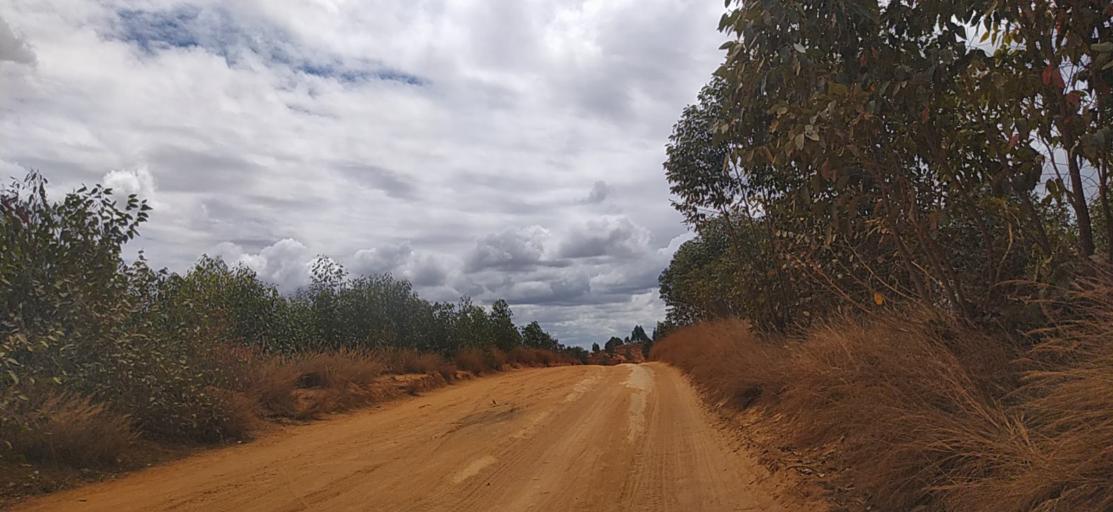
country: MG
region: Alaotra Mangoro
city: Ambatondrazaka
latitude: -18.0629
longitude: 48.2571
